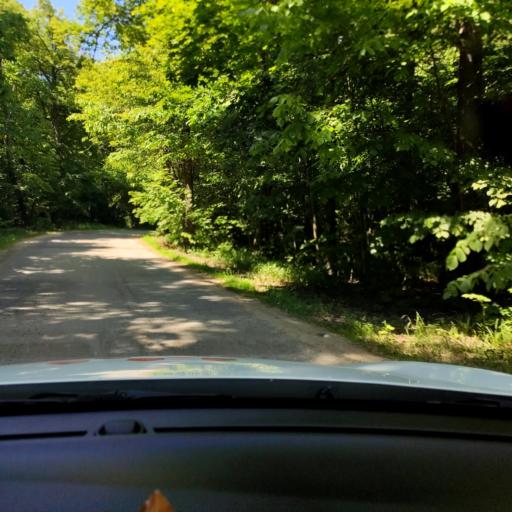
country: RU
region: Tatarstan
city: Osinovo
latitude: 55.7788
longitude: 48.7965
